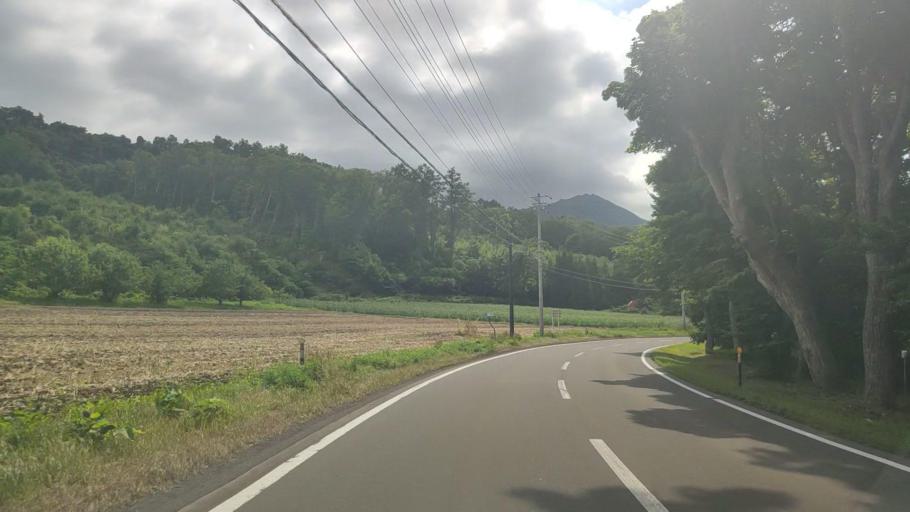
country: JP
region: Hokkaido
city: Date
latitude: 42.5579
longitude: 140.8758
